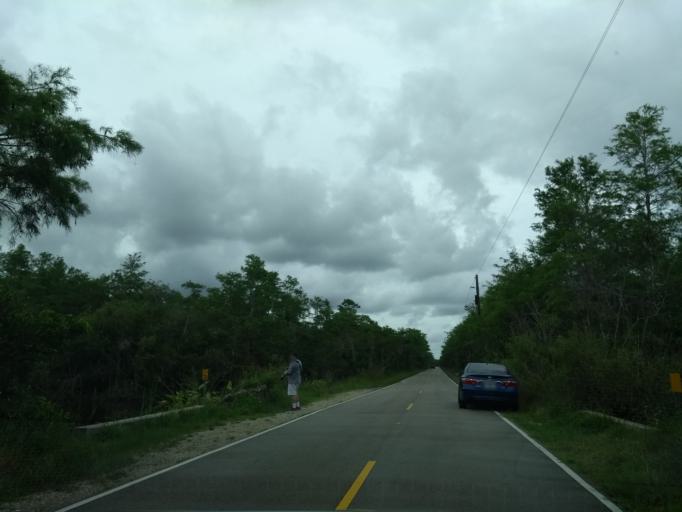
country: US
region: Florida
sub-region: Miami-Dade County
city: The Hammocks
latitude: 25.7613
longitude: -80.9103
